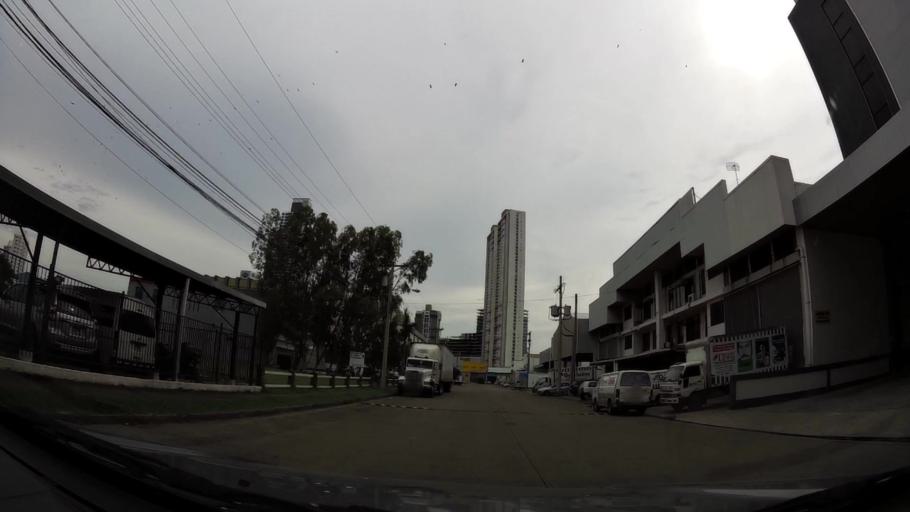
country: PA
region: Panama
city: San Miguelito
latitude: 9.0123
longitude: -79.4811
